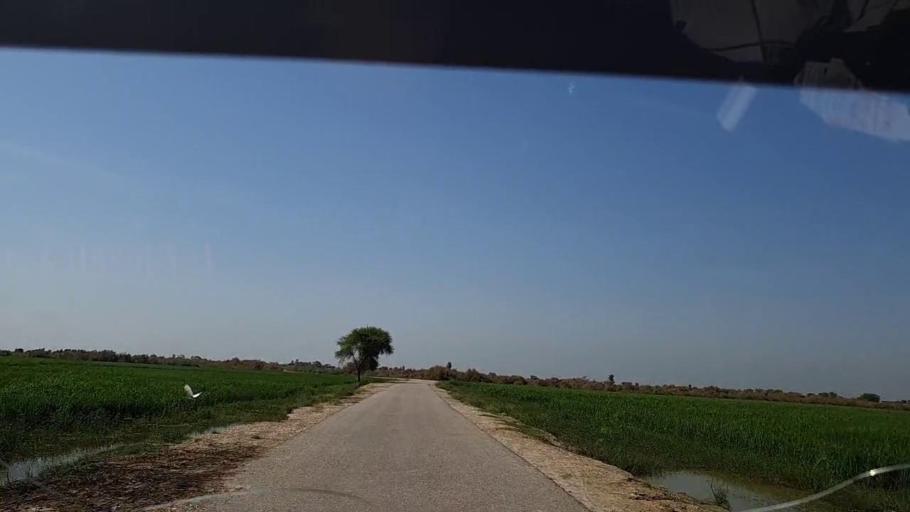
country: PK
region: Sindh
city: Kandhkot
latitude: 28.3122
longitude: 69.1007
